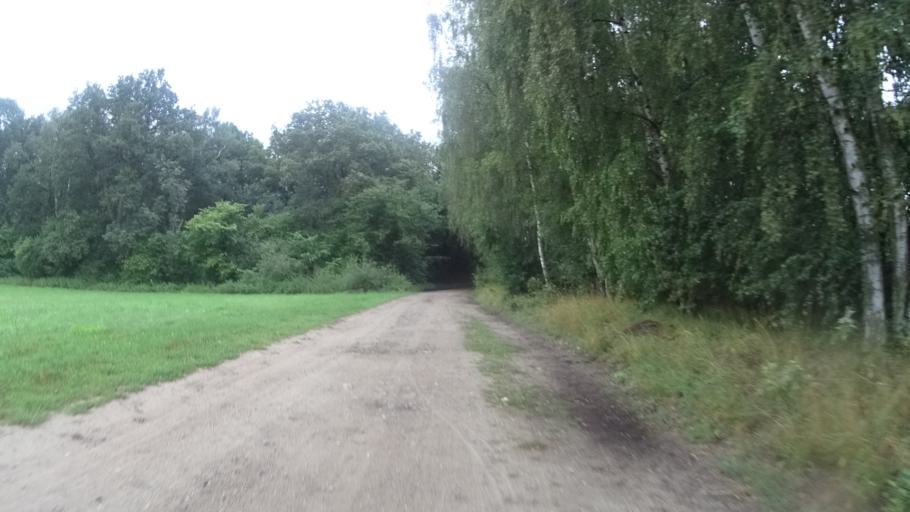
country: DE
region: Schleswig-Holstein
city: Dalldorf
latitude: 53.4148
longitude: 10.6107
